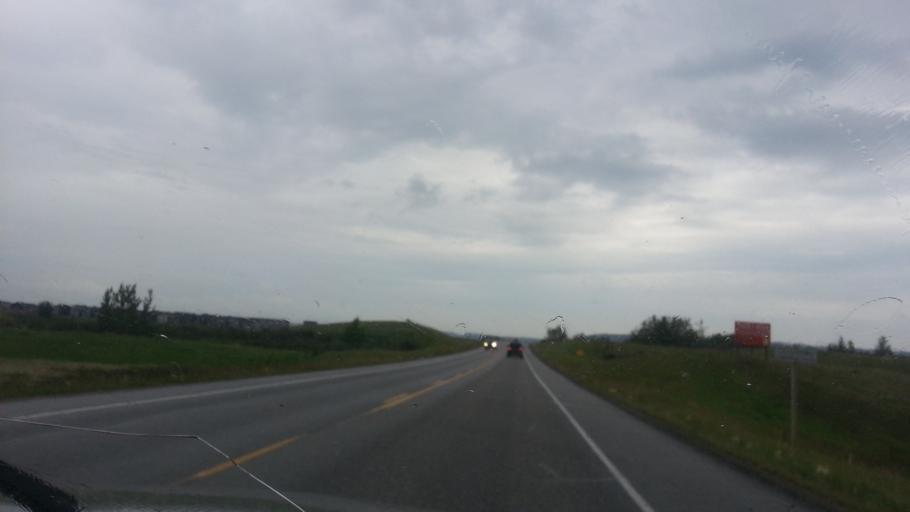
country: CA
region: Alberta
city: Cochrane
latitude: 51.1494
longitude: -114.4668
